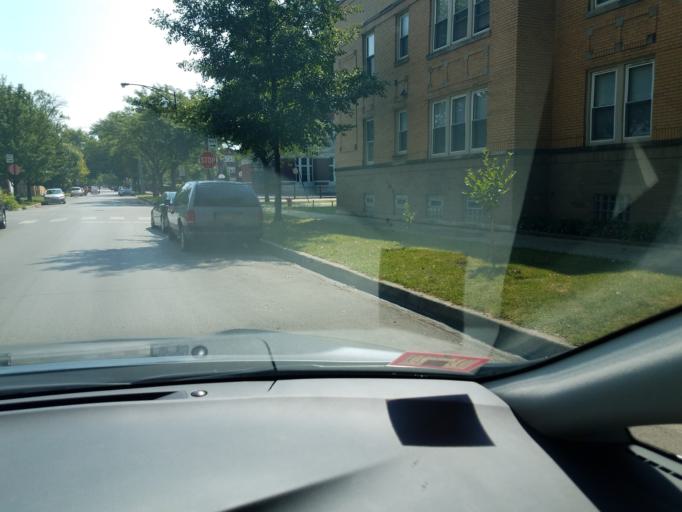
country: US
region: Illinois
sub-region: Cook County
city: Lincolnwood
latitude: 41.9646
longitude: -87.7249
